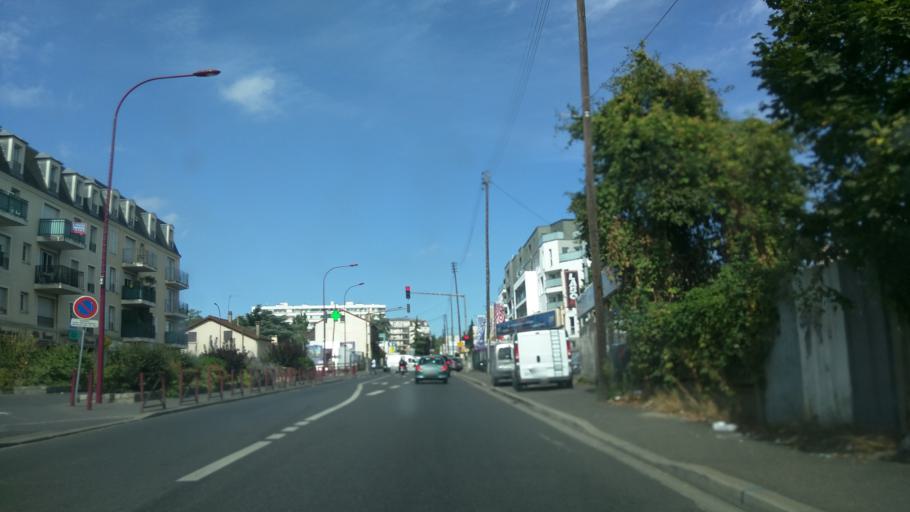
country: FR
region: Ile-de-France
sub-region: Departement du Val-d'Oise
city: Bezons
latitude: 48.9336
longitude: 2.2098
